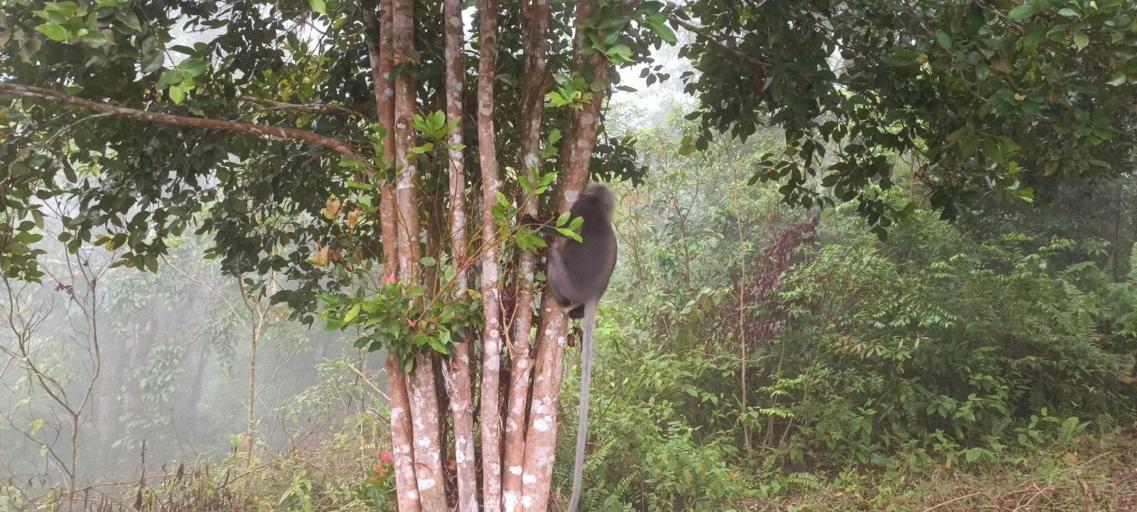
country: MY
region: Perak
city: Taiping
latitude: 4.8668
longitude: 100.7768
